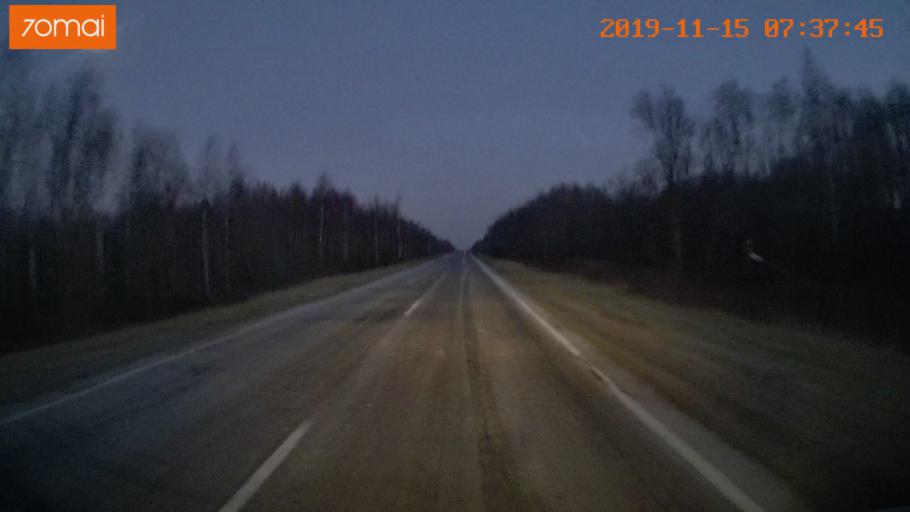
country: RU
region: Vologda
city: Sheksna
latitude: 58.7489
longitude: 38.4189
